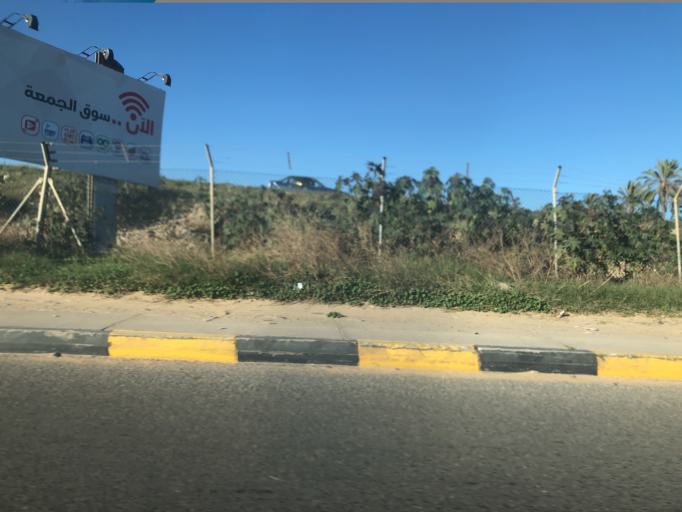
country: LY
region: Tripoli
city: Tripoli
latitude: 32.8702
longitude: 13.2666
